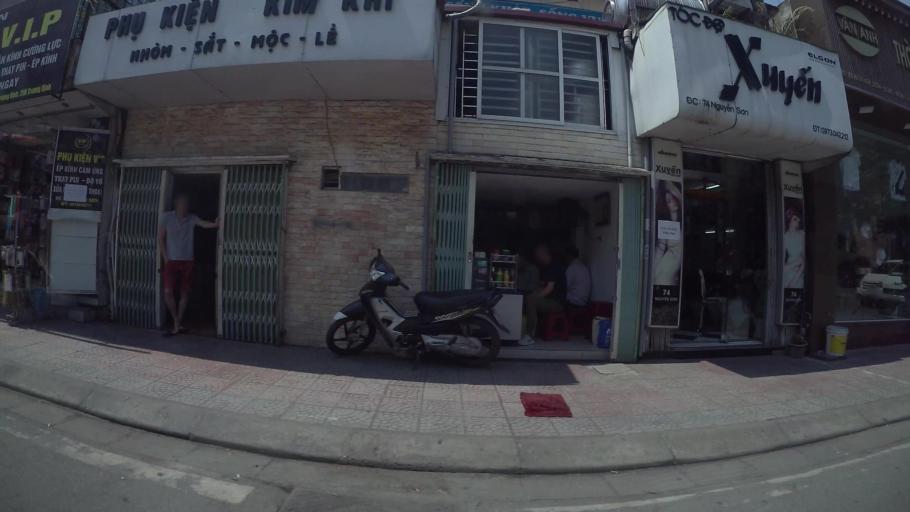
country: VN
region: Ha Noi
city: Hoan Kiem
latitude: 21.0478
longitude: 105.8763
